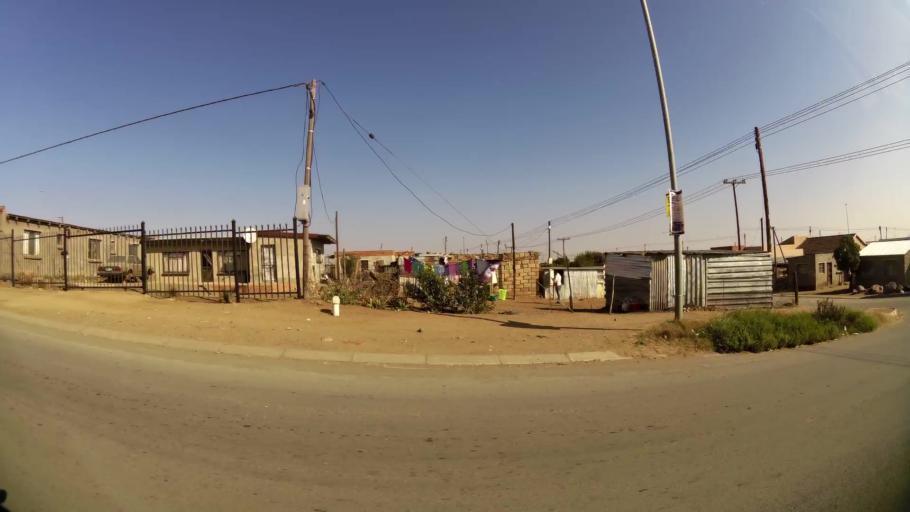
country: ZA
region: Orange Free State
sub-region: Mangaung Metropolitan Municipality
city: Bloemfontein
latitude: -29.1738
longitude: 26.2407
